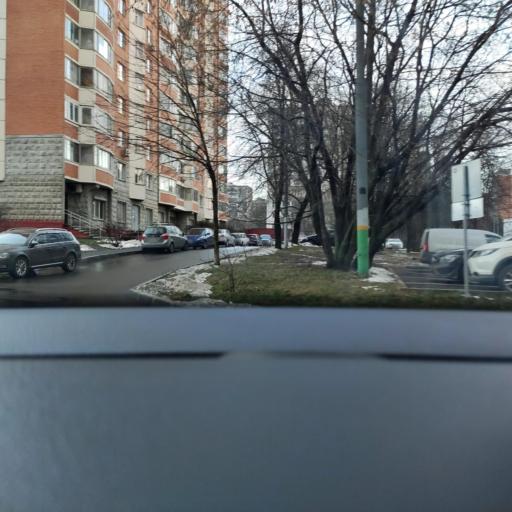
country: RU
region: Moscow
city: Vatutino
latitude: 55.8933
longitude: 37.6546
